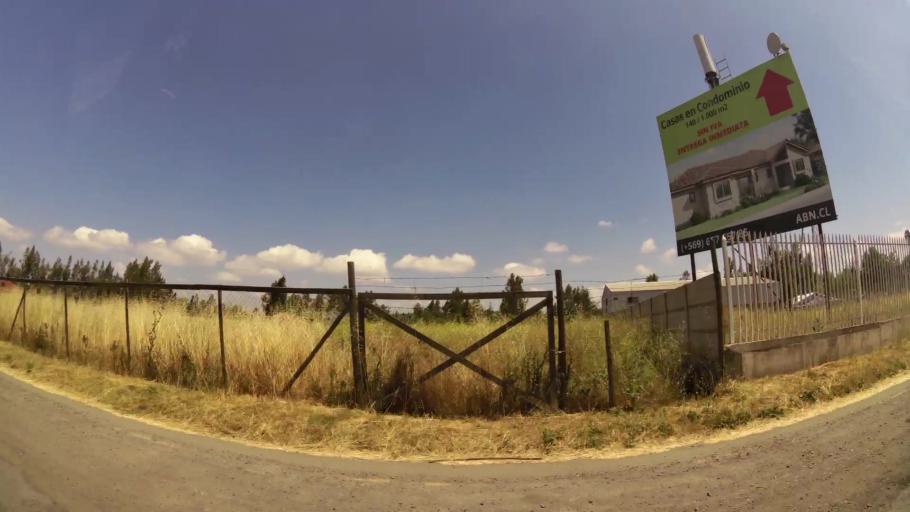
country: CL
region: Santiago Metropolitan
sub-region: Provincia de Maipo
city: San Bernardo
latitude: -33.5795
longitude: -70.7739
